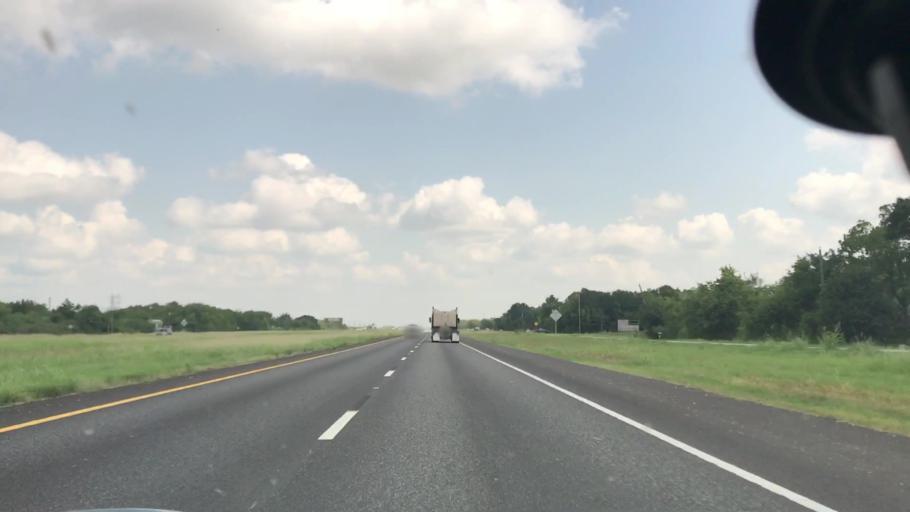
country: US
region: Texas
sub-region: Brazoria County
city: Rosharon
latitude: 29.3941
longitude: -95.4267
